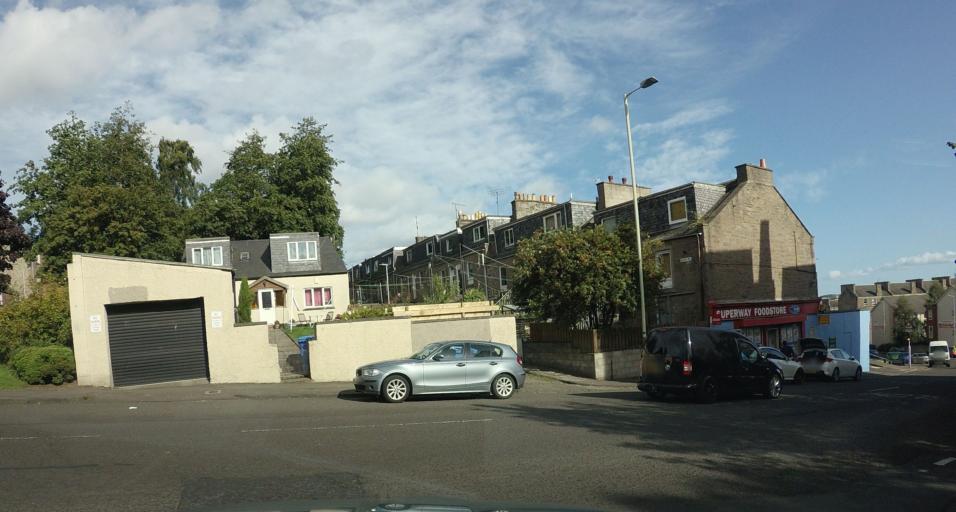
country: GB
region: Scotland
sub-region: Dundee City
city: Dundee
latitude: 56.4629
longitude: -2.9969
